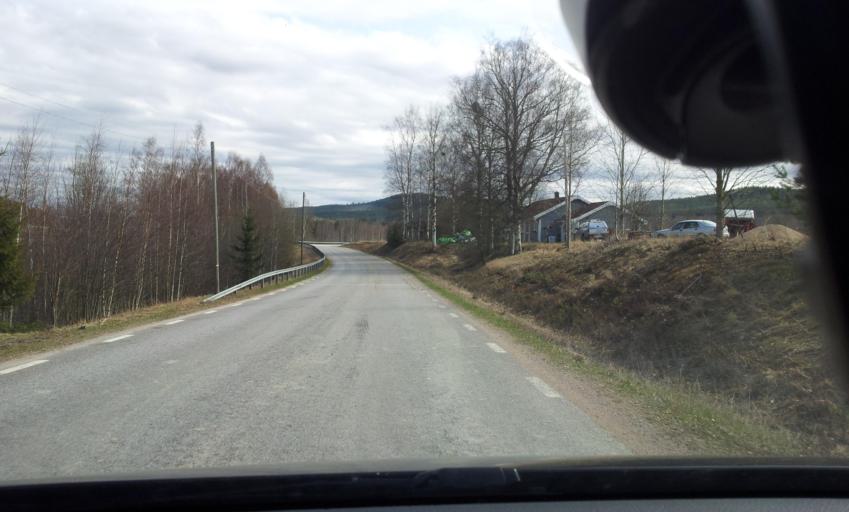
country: SE
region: Gaevleborg
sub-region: Ljusdals Kommun
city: Farila
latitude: 61.7753
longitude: 15.9527
